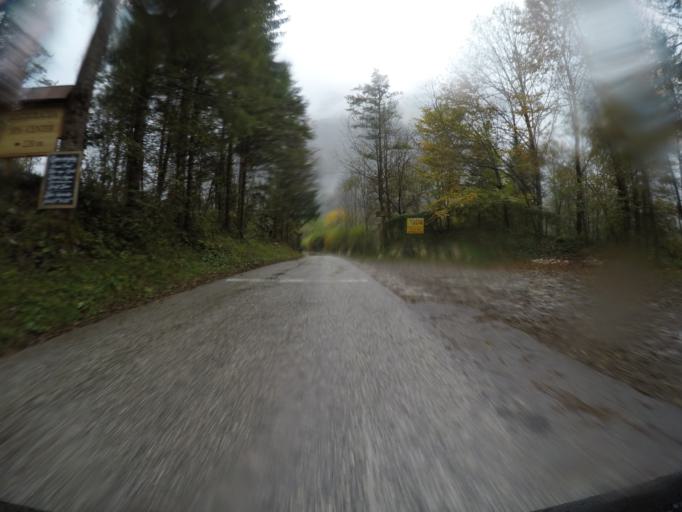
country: SI
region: Bovec
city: Bovec
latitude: 46.3316
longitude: 13.6440
